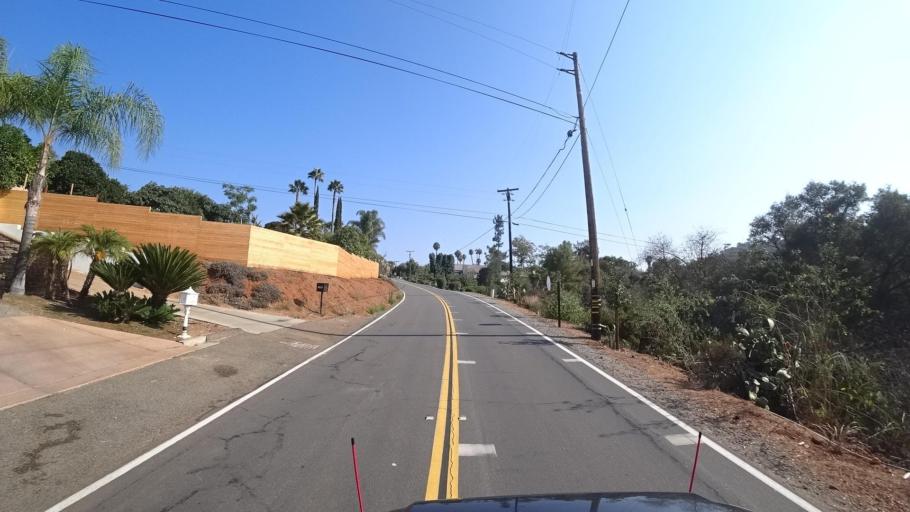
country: US
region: California
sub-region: San Diego County
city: Vista
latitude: 33.2262
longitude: -117.2152
